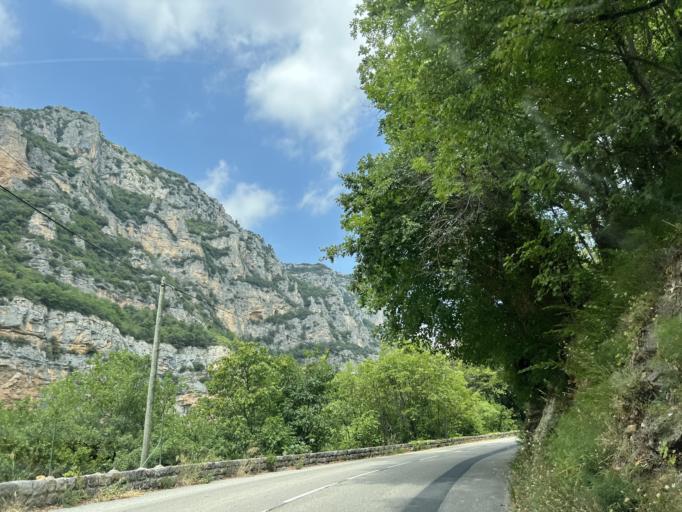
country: FR
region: Provence-Alpes-Cote d'Azur
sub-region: Departement des Alpes-Maritimes
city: Le Rouret
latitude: 43.7212
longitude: 6.9935
